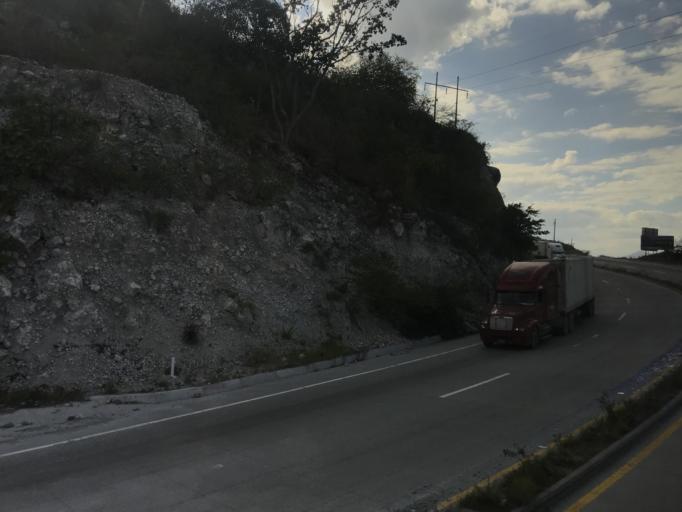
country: GT
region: El Progreso
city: Guastatoya
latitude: 14.8512
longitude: -90.1056
